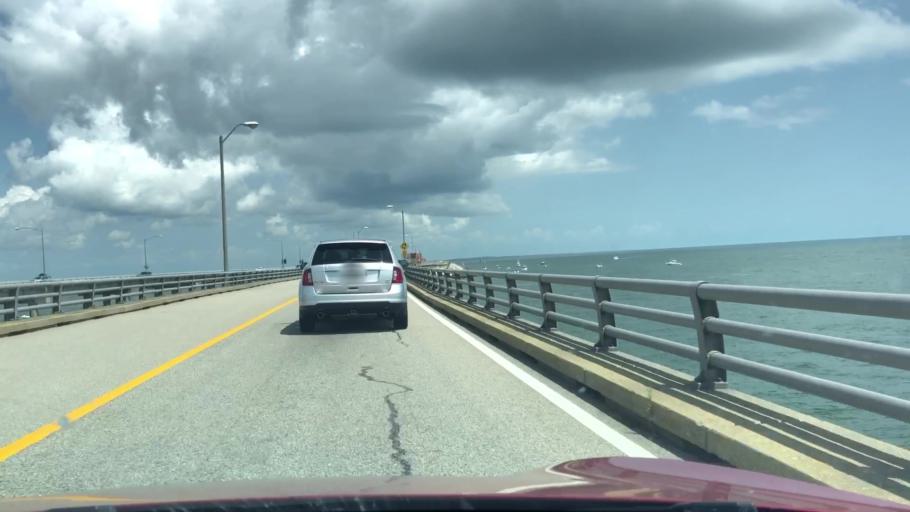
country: US
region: Virginia
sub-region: City of Virginia Beach
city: Virginia Beach
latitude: 37.0311
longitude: -76.0840
